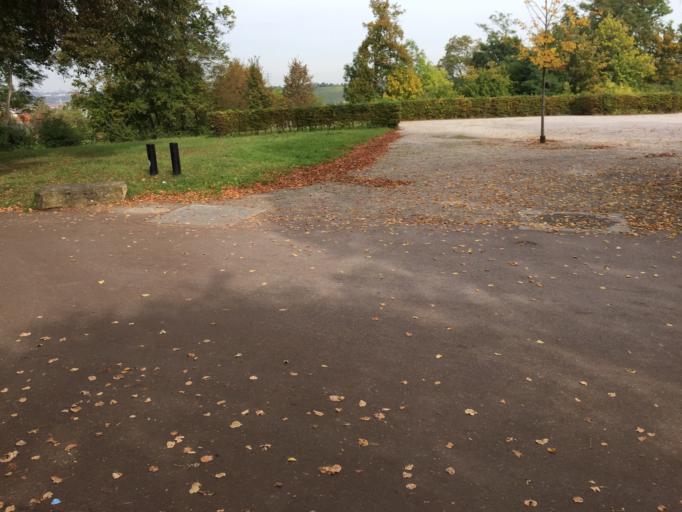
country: DE
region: Baden-Wuerttemberg
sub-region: Regierungsbezirk Stuttgart
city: Stuttgart Feuerbach
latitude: 48.8084
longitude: 9.1719
